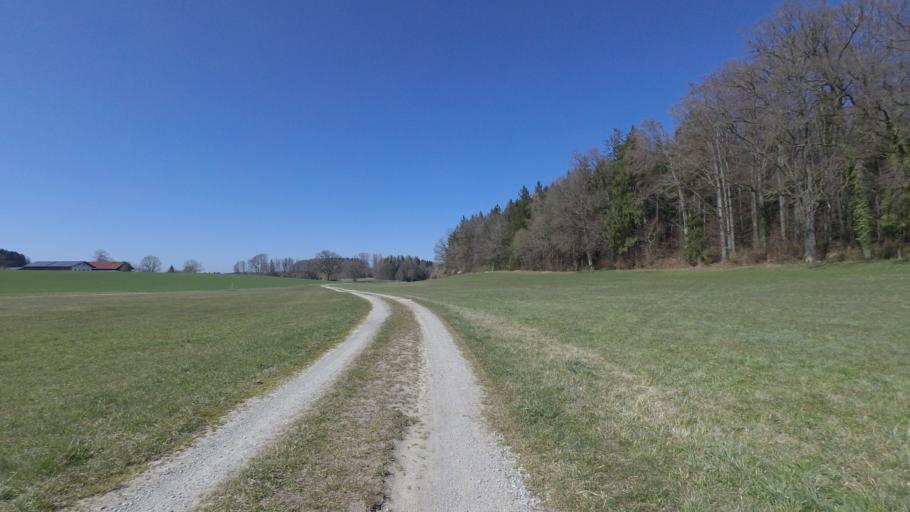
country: DE
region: Bavaria
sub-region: Upper Bavaria
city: Seeon-Seebruck
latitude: 47.9368
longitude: 12.5042
